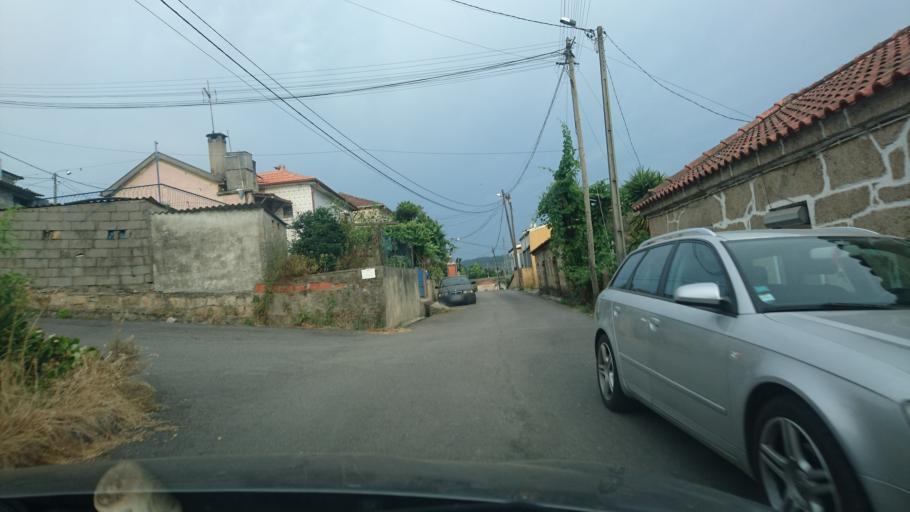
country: PT
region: Porto
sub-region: Paredes
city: Recarei
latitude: 41.1565
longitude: -8.4044
